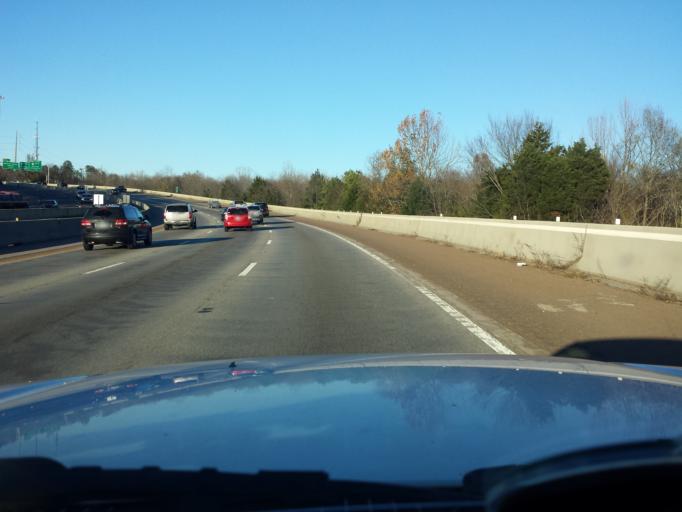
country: US
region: Mississippi
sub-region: Rankin County
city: Flowood
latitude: 32.3150
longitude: -90.1585
